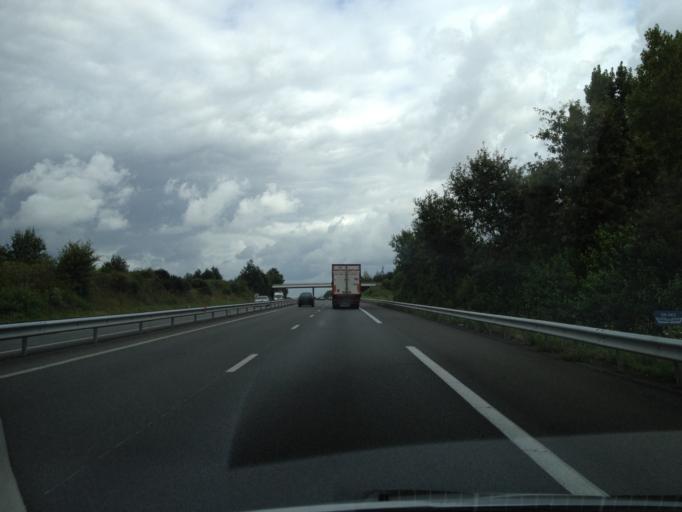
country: FR
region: Pays de la Loire
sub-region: Departement de la Vendee
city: Bournezeau
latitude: 46.6762
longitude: -1.1559
